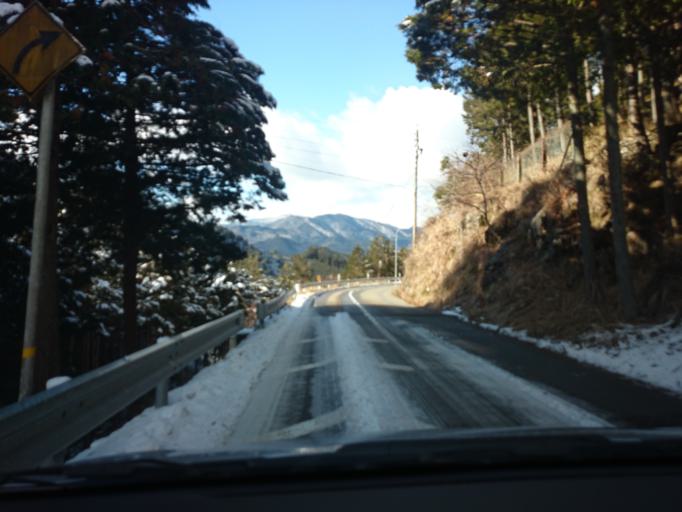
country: JP
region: Gifu
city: Gujo
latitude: 35.7472
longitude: 136.9771
